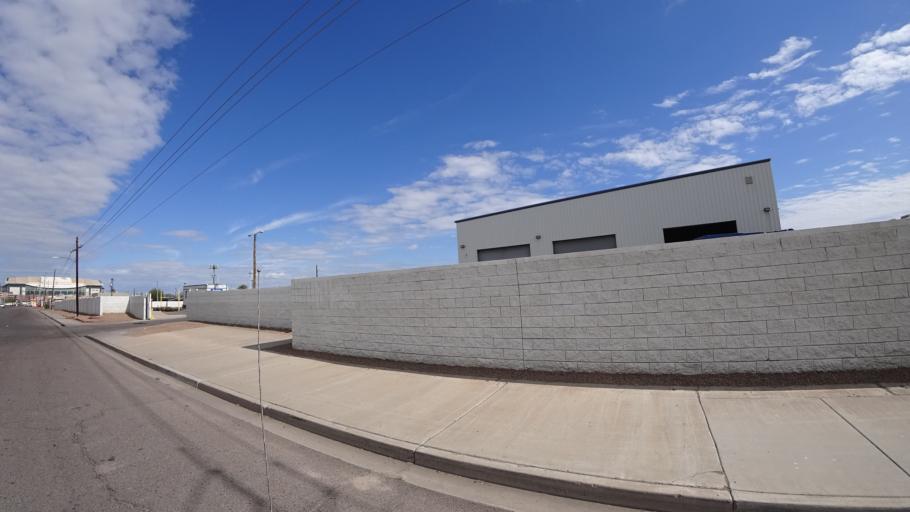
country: US
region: Arizona
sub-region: Maricopa County
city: Phoenix
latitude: 33.4342
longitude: -112.0674
